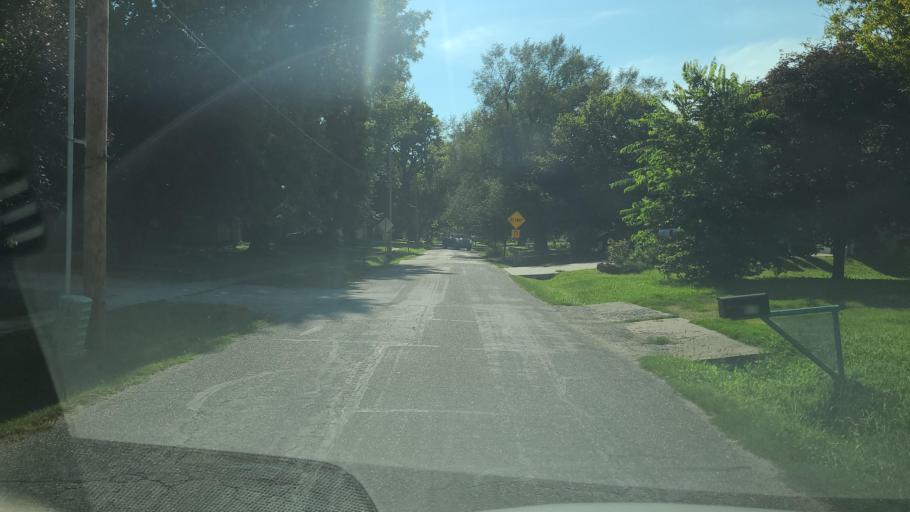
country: US
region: Kansas
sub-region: Douglas County
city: Lawrence
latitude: 38.9806
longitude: -95.2263
